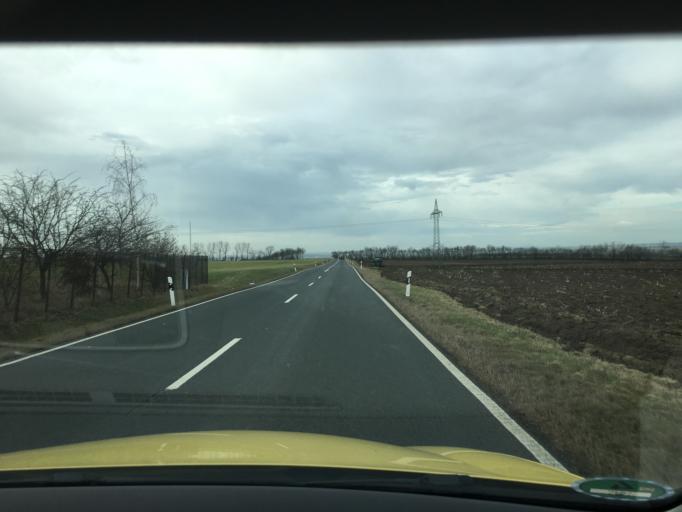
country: DE
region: Thuringia
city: Ballstedt
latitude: 51.0499
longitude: 11.2067
